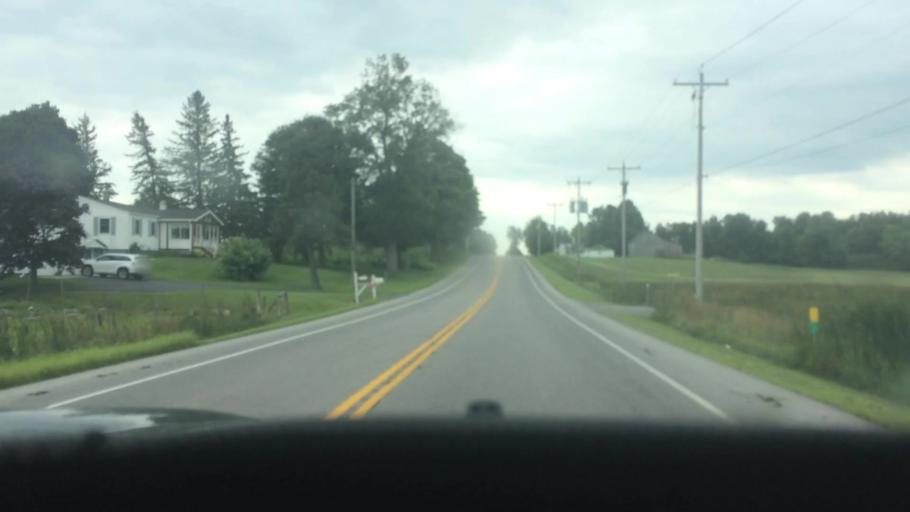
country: US
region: New York
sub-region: St. Lawrence County
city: Ogdensburg
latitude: 44.6111
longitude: -75.3984
